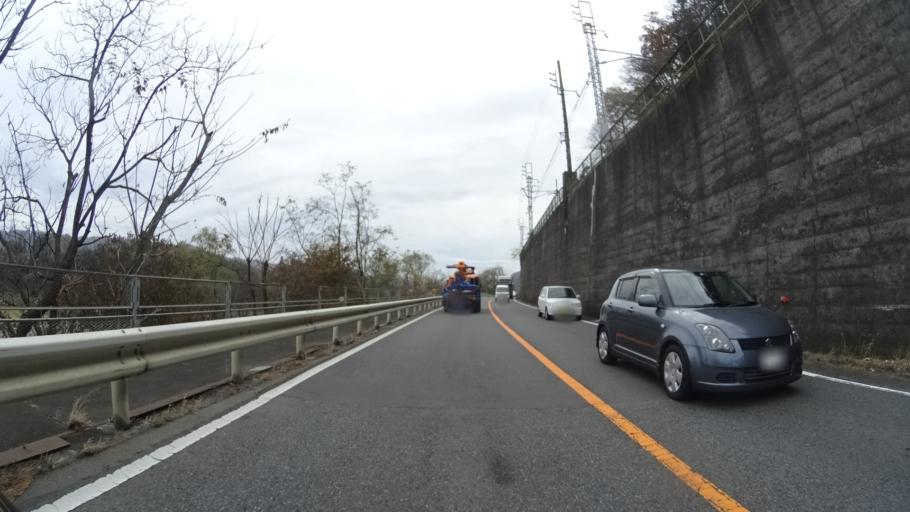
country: JP
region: Gunma
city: Numata
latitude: 36.6171
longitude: 139.0418
